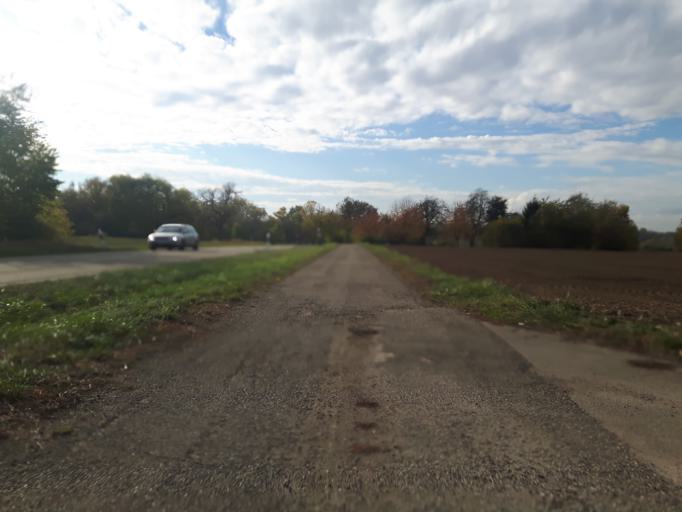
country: DE
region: Baden-Wuerttemberg
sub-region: Karlsruhe Region
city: Malsch
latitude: 49.2606
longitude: 8.6717
